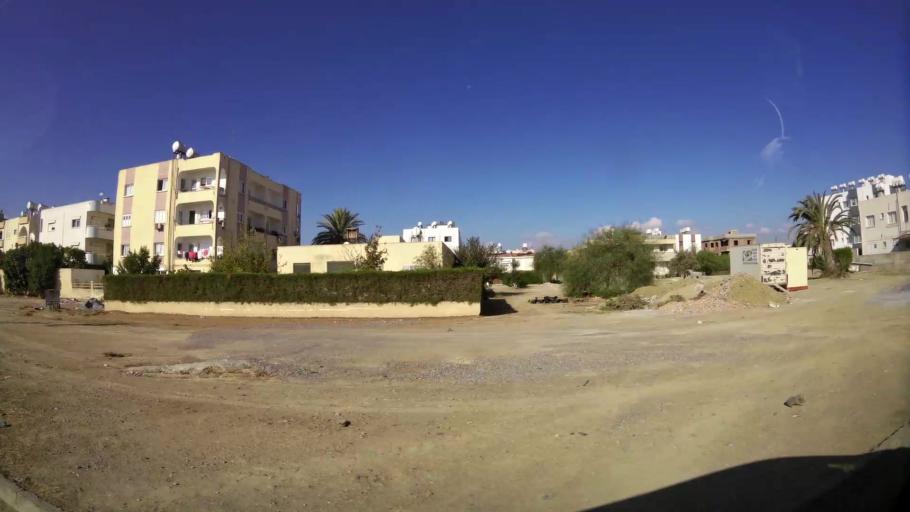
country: CY
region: Lefkosia
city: Nicosia
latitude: 35.2101
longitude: 33.3090
